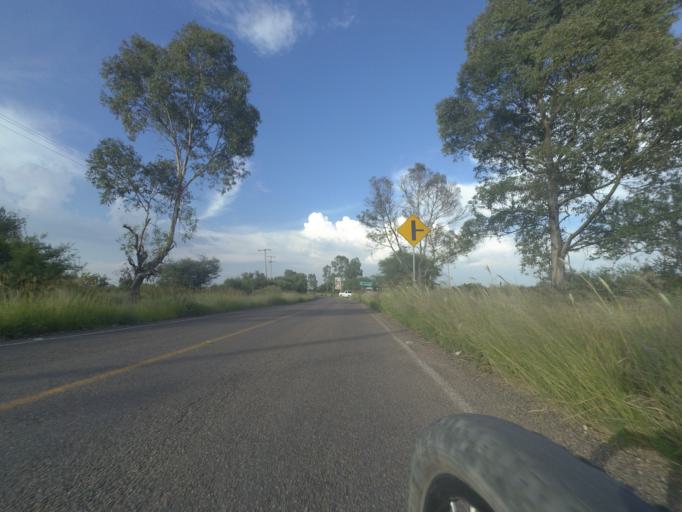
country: MX
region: Aguascalientes
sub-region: Aguascalientes
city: Penuelas (El Cienegal)
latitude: 21.7190
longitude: -102.3664
